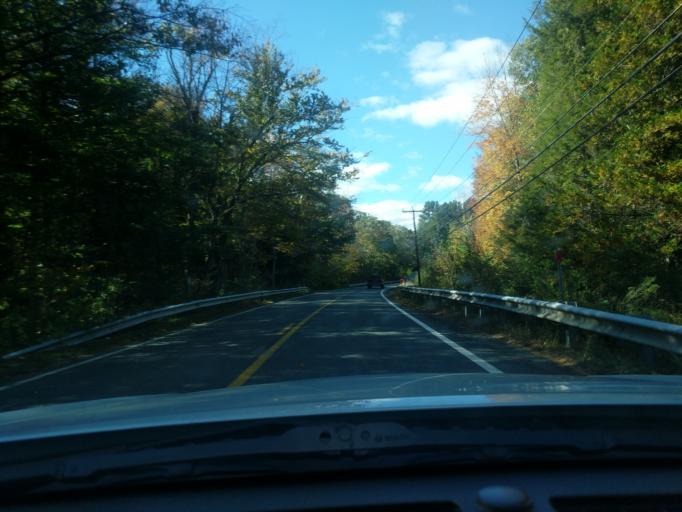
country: US
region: Massachusetts
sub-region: Hampden County
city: Granville
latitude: 42.1671
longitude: -72.8683
